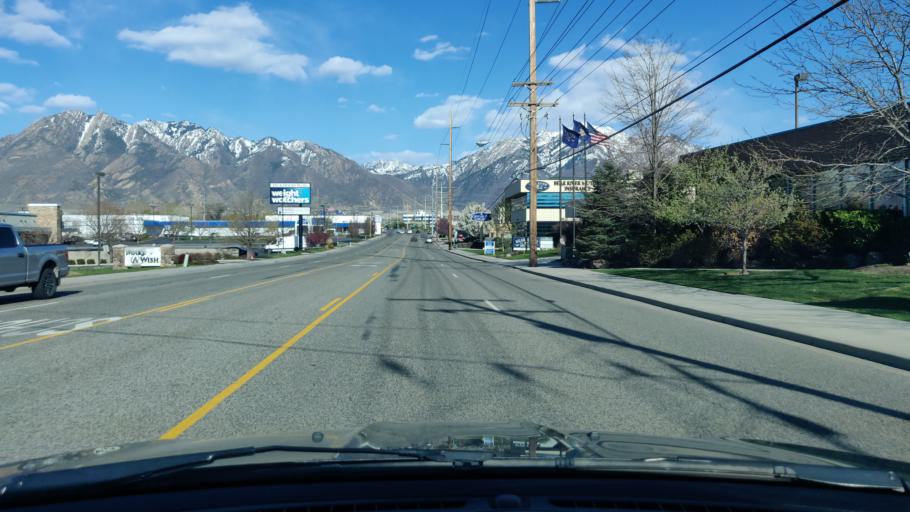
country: US
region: Utah
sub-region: Salt Lake County
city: Midvale
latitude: 40.6318
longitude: -111.8706
